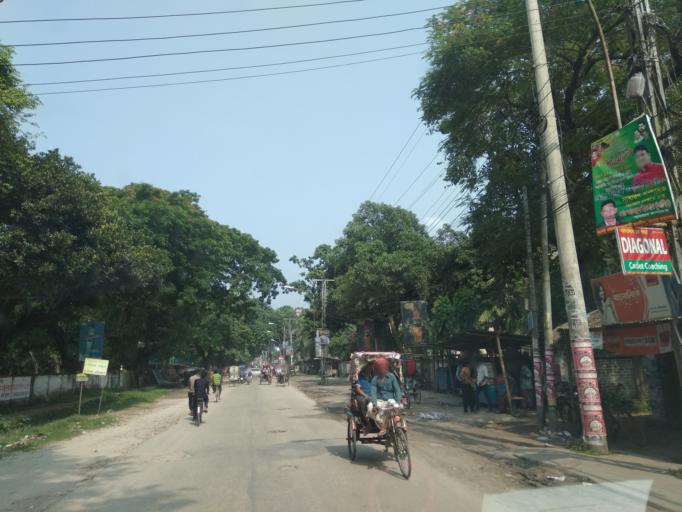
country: BD
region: Rangpur Division
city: Rangpur
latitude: 25.7582
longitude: 89.2358
